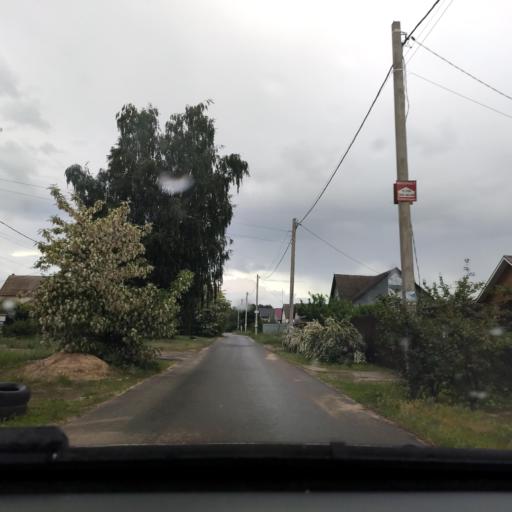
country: RU
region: Voronezj
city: Podgornoye
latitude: 51.7917
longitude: 39.1516
